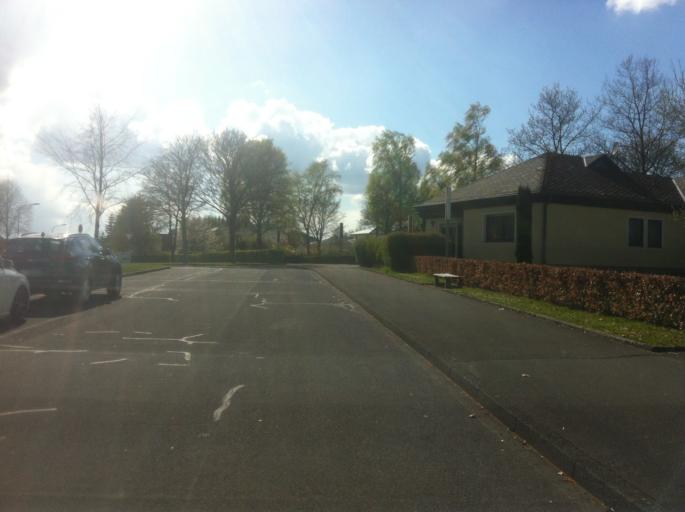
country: DE
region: Rheinland-Pfalz
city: Irrhausen
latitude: 50.0717
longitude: 6.1891
